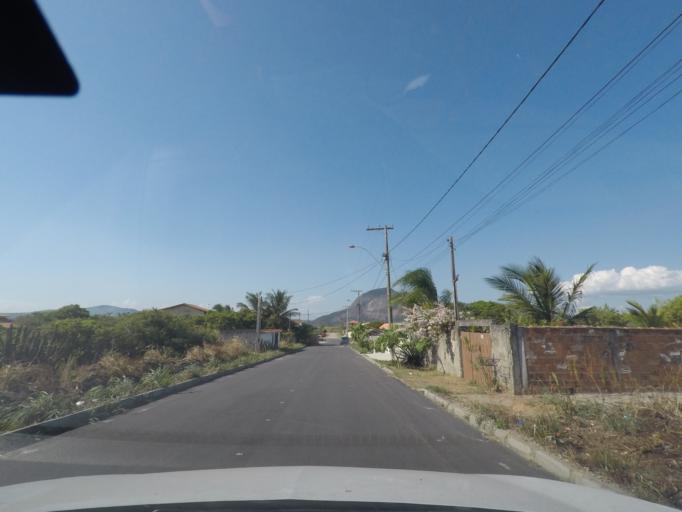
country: BR
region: Rio de Janeiro
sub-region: Marica
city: Marica
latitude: -22.9679
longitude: -42.9182
